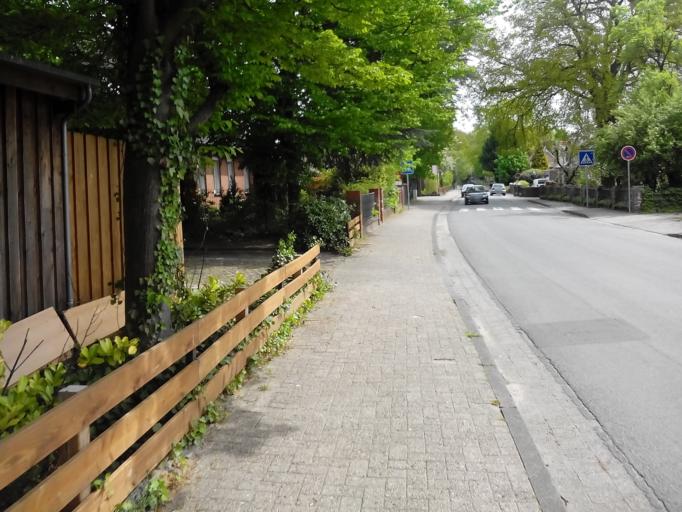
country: DE
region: Lower Saxony
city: Verden
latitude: 52.9199
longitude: 9.2544
